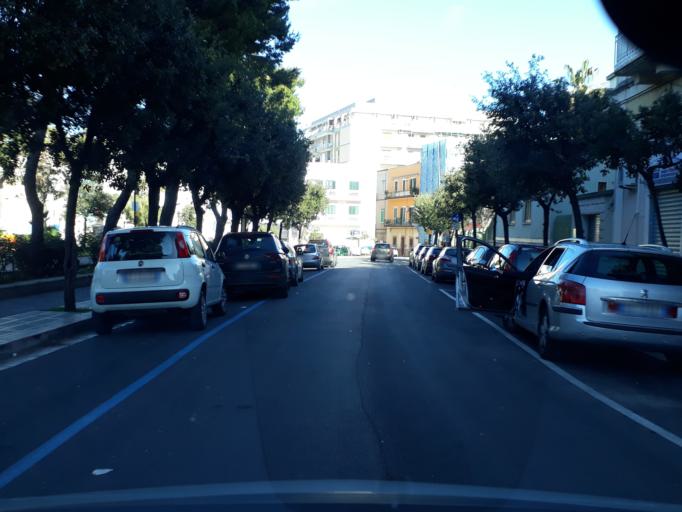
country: IT
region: Apulia
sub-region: Provincia di Bari
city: Monopoli
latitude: 40.9525
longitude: 17.2954
